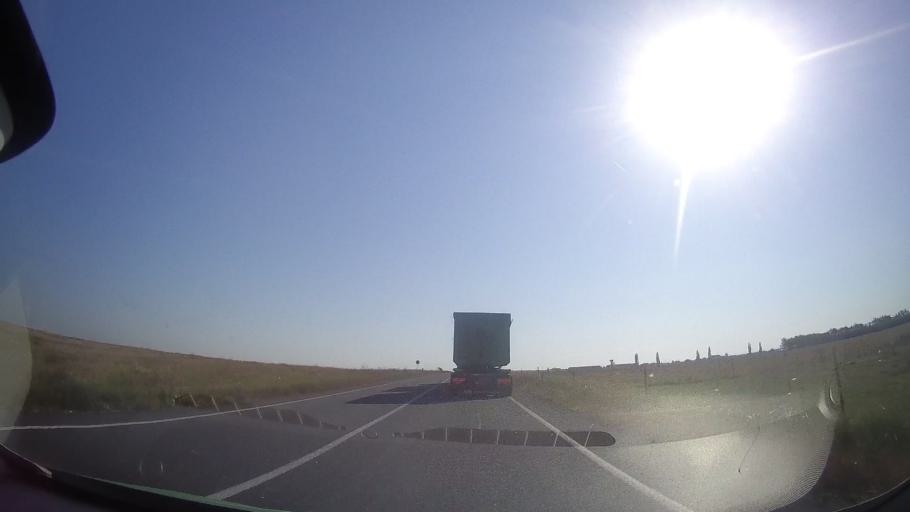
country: RO
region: Timis
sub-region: Comuna Ghizela
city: Ghizela
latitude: 45.7764
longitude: 21.6924
